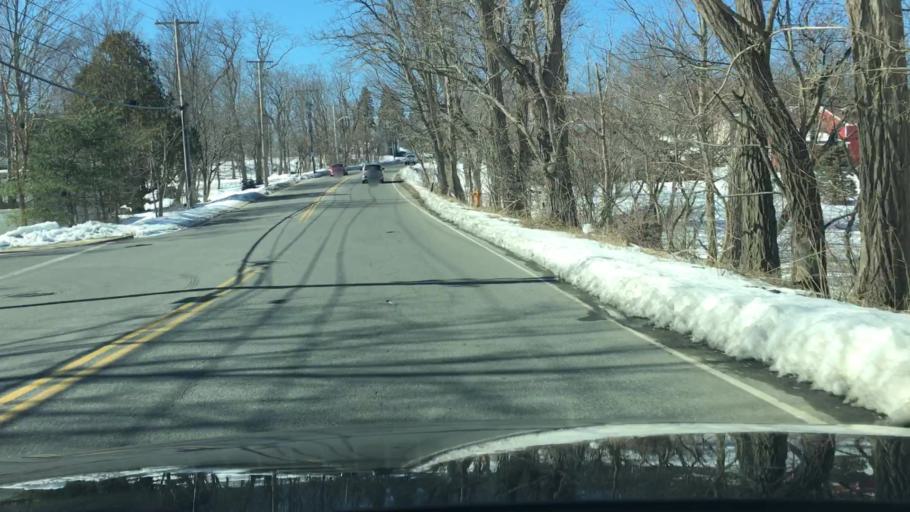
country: US
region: Massachusetts
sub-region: Essex County
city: Amesbury
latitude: 42.8488
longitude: -70.9088
